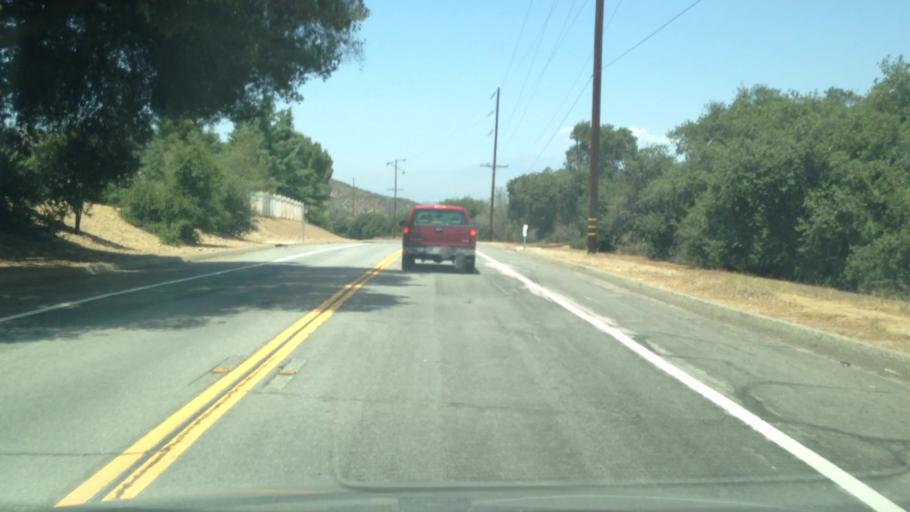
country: US
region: California
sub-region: Riverside County
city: Cherry Valley
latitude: 34.0081
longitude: -116.9816
